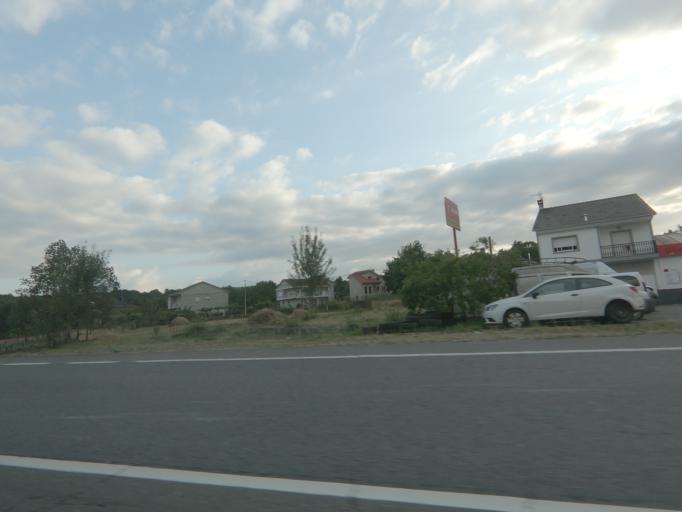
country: ES
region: Galicia
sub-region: Provincia de Ourense
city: Taboadela
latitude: 42.2810
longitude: -7.8386
